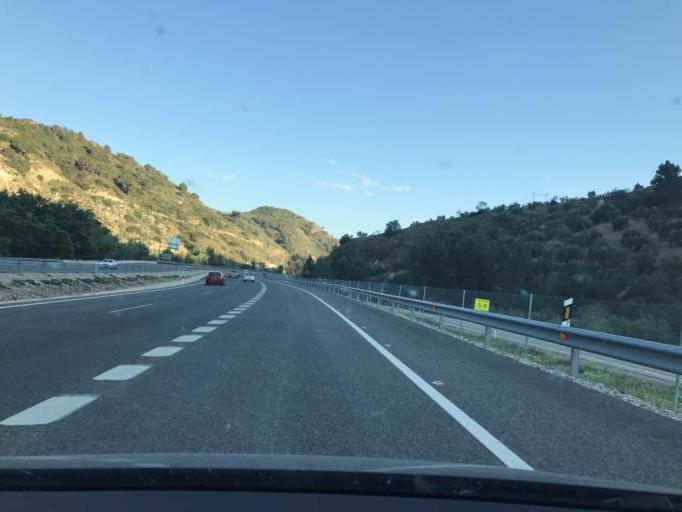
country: ES
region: Andalusia
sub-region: Provincia de Jaen
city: Cambil
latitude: 37.6735
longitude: -3.6235
